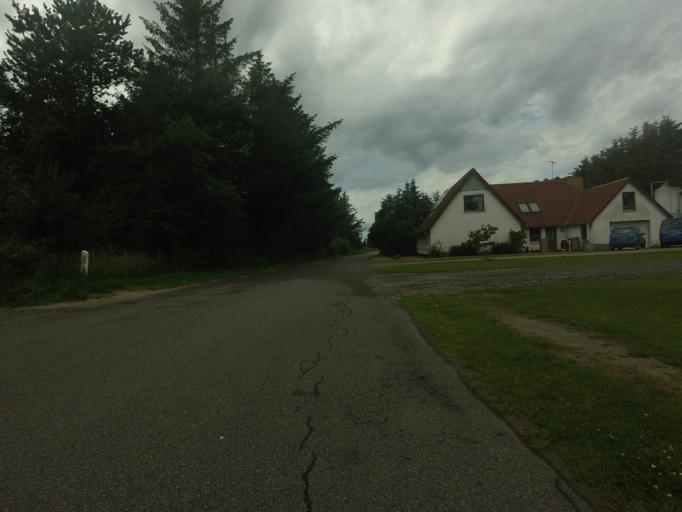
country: DK
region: North Denmark
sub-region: Jammerbugt Kommune
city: Pandrup
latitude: 57.3653
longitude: 9.7353
